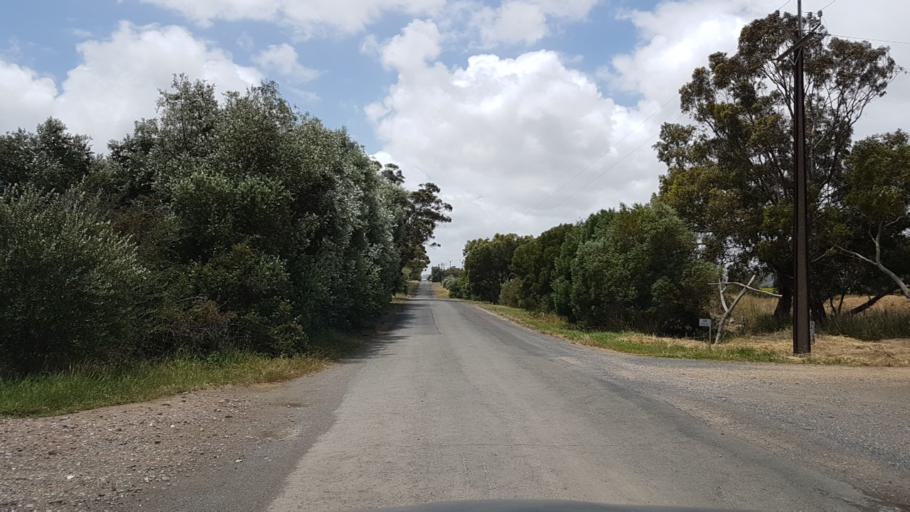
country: AU
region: South Australia
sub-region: Onkaparinga
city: McLaren Vale
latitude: -35.2407
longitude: 138.5389
